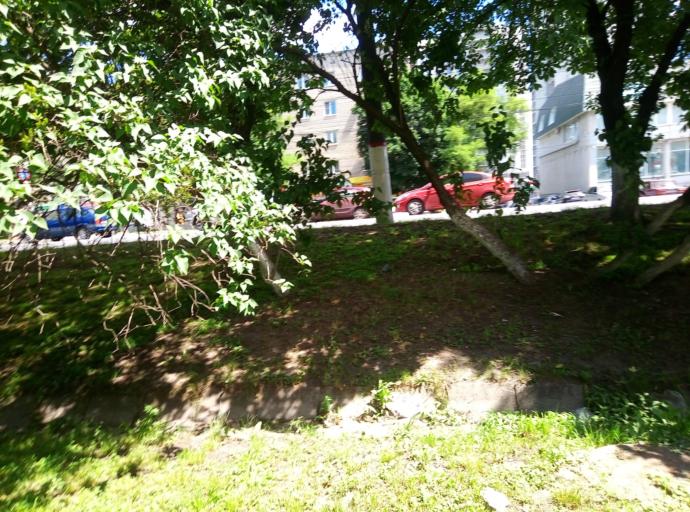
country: RU
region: Kursk
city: Kursk
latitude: 51.7536
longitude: 36.1898
